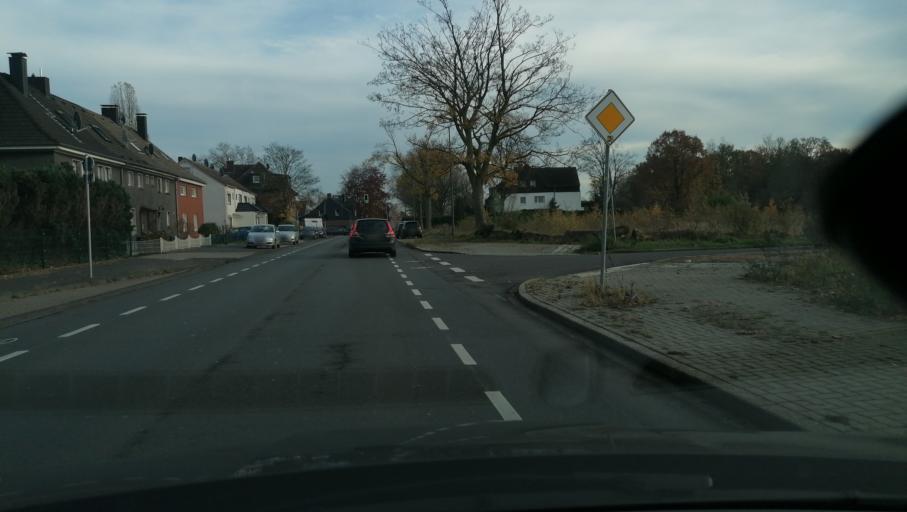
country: DE
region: North Rhine-Westphalia
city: Castrop-Rauxel
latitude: 51.5856
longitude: 7.3413
